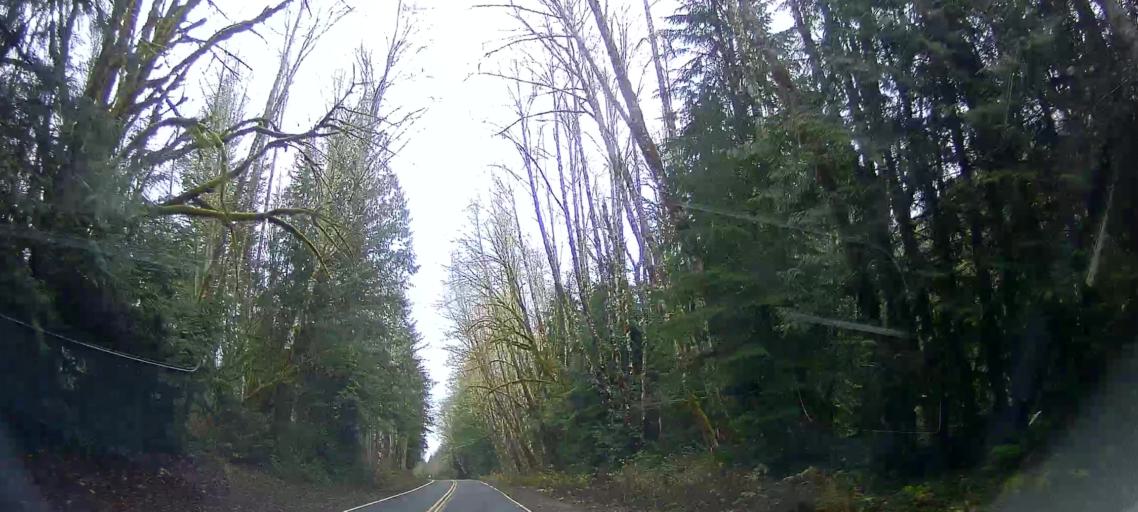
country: US
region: Washington
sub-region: Snohomish County
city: Darrington
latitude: 48.5005
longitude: -121.4619
